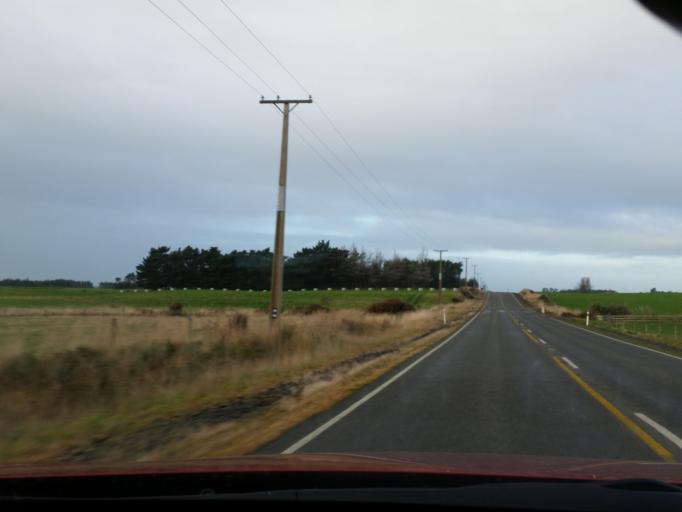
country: NZ
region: Southland
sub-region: Invercargill City
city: Invercargill
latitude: -46.4506
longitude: 168.5107
